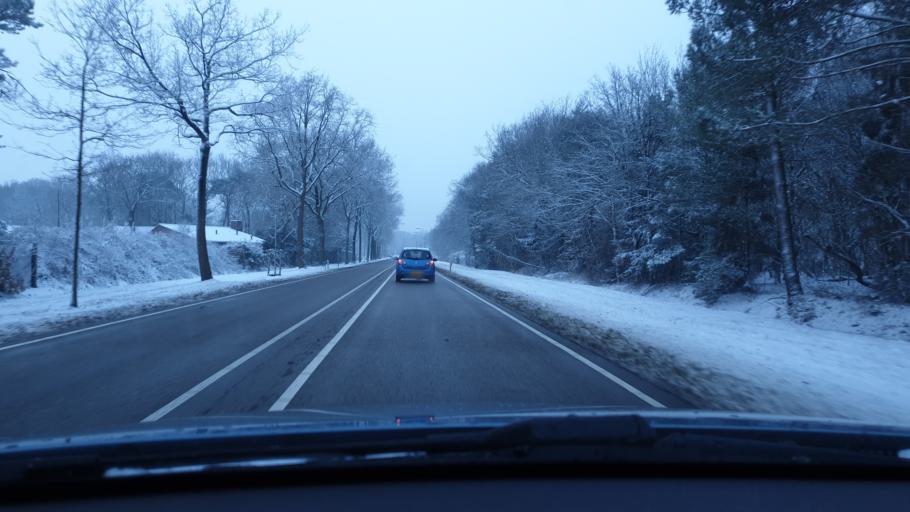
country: NL
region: North Brabant
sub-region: Gemeente Landerd
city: Zeeland
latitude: 51.6907
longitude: 5.6633
